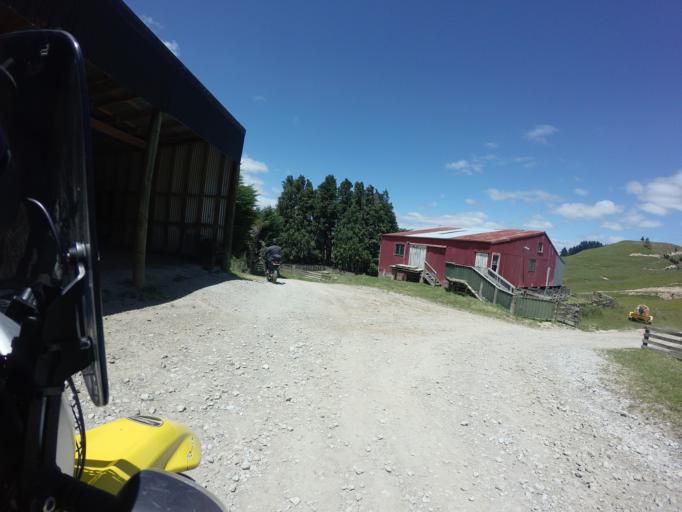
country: NZ
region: Gisborne
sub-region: Gisborne District
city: Gisborne
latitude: -38.4913
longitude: 177.5603
